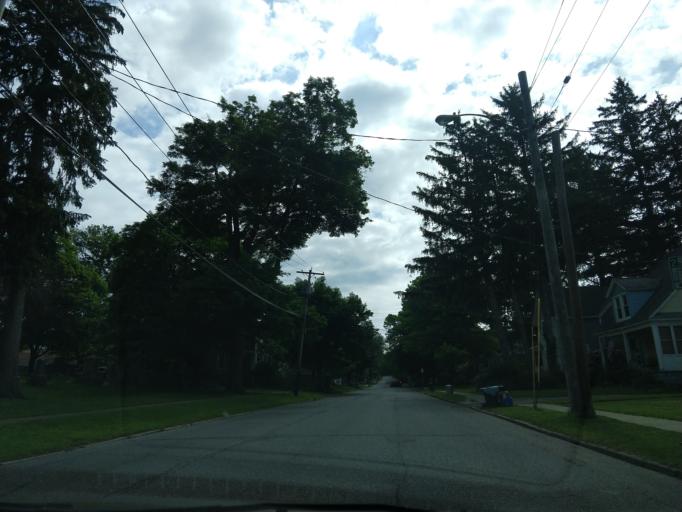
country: US
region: New York
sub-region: Erie County
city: East Aurora
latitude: 42.7656
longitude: -78.6097
